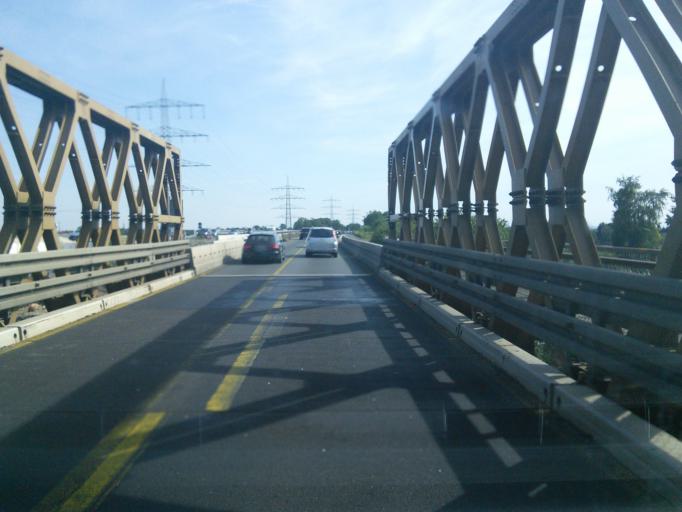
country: DE
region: North Rhine-Westphalia
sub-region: Regierungsbezirk Dusseldorf
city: Dormagen
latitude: 51.1133
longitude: 6.7995
